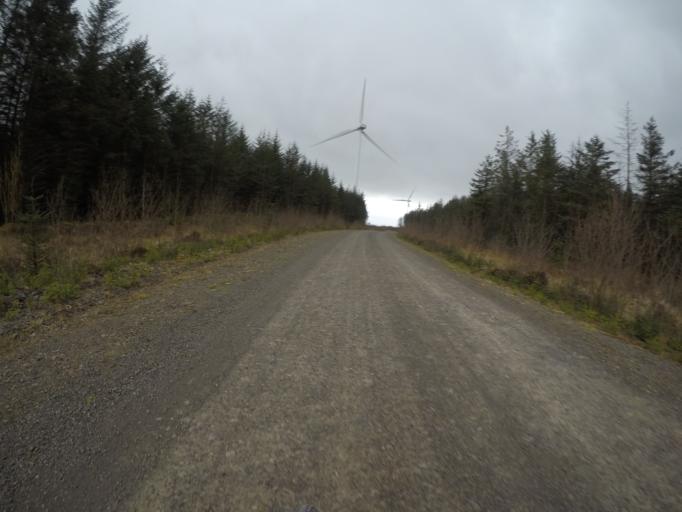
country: GB
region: Scotland
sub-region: East Ayrshire
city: Newmilns
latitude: 55.6769
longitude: -4.3354
